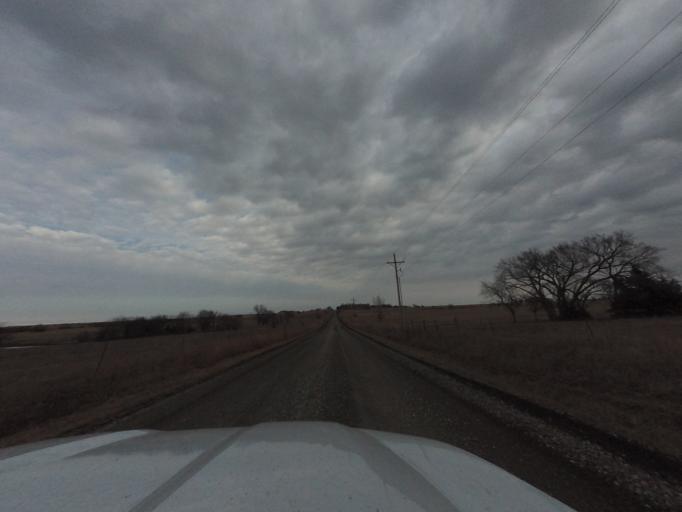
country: US
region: Kansas
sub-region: Chase County
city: Cottonwood Falls
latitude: 38.4419
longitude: -96.3731
